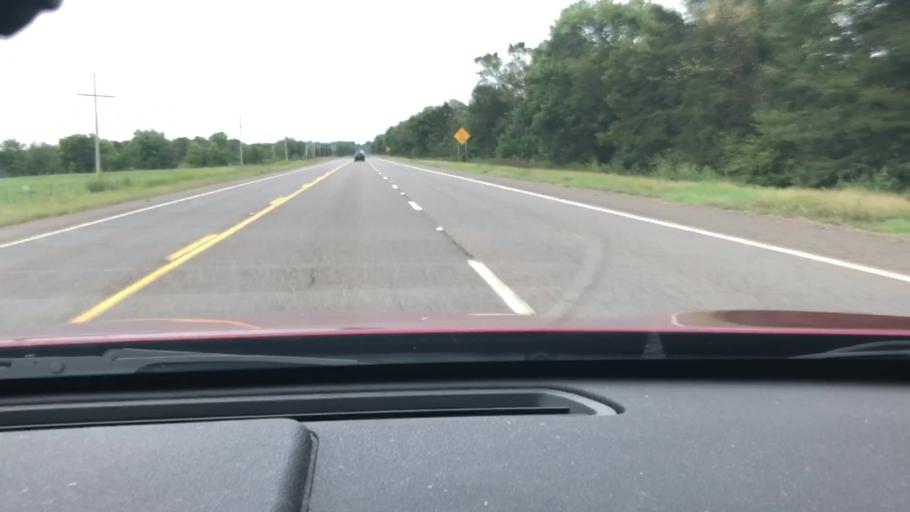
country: US
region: Arkansas
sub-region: Lafayette County
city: Lewisville
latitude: 33.3562
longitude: -93.6485
